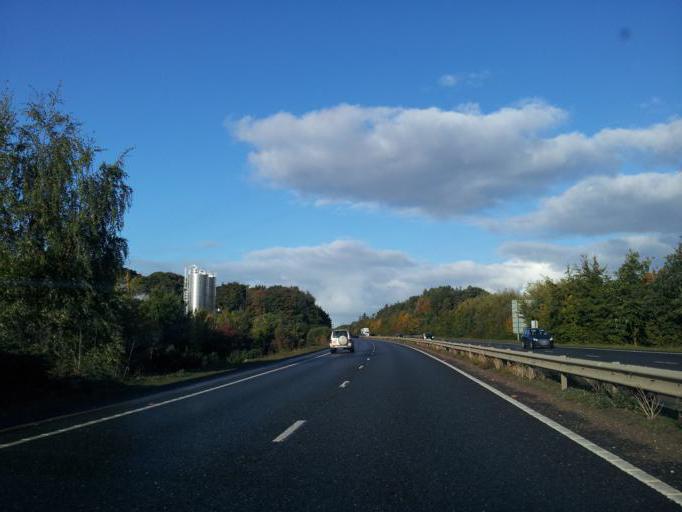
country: GB
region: England
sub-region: Norfolk
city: Costessey
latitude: 52.6535
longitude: 1.1769
